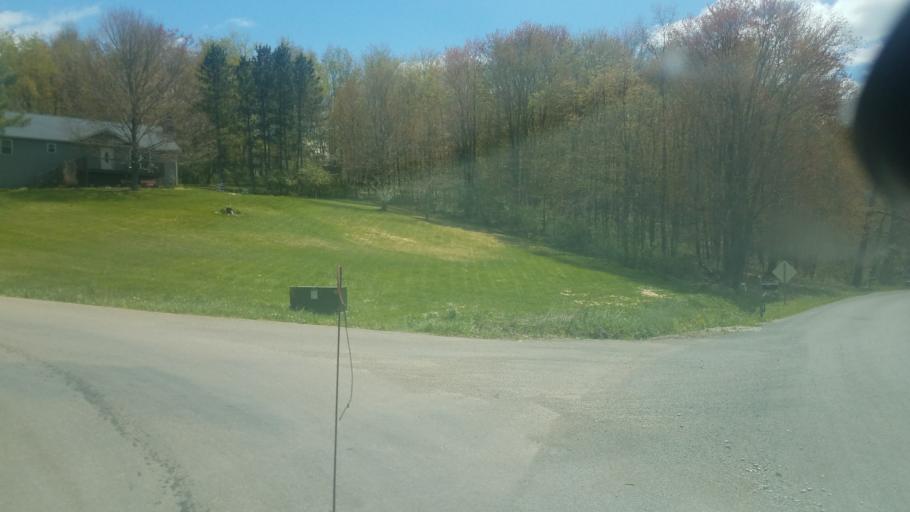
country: US
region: Ohio
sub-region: Knox County
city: Gambier
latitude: 40.4384
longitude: -82.3660
